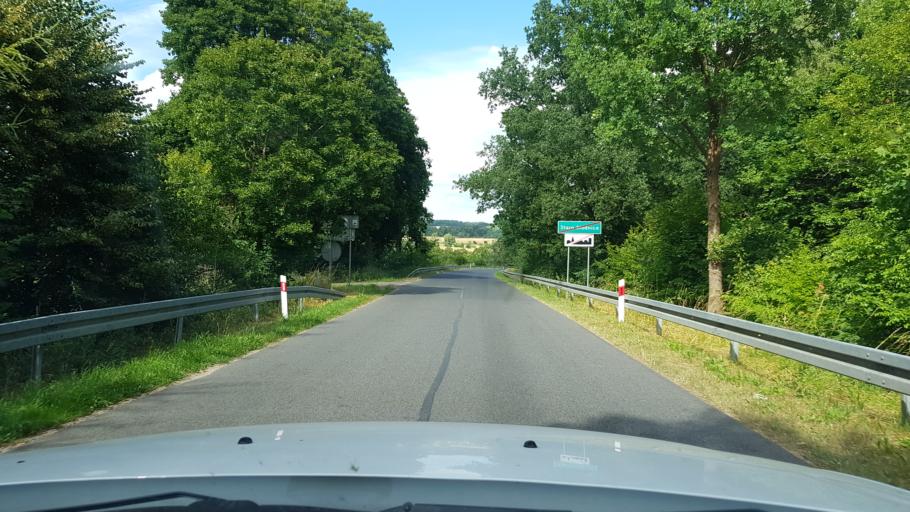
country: PL
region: West Pomeranian Voivodeship
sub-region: Powiat drawski
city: Kalisz Pomorski
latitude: 53.3943
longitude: 15.9584
